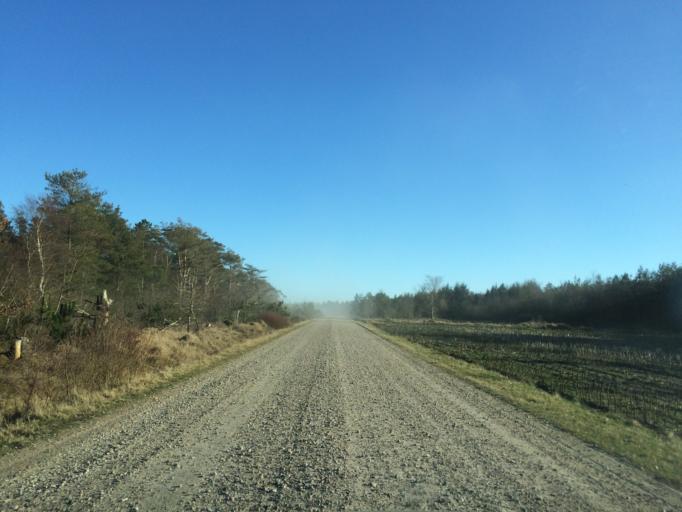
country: DK
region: Central Jutland
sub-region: Holstebro Kommune
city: Ulfborg
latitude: 56.2853
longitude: 8.3891
